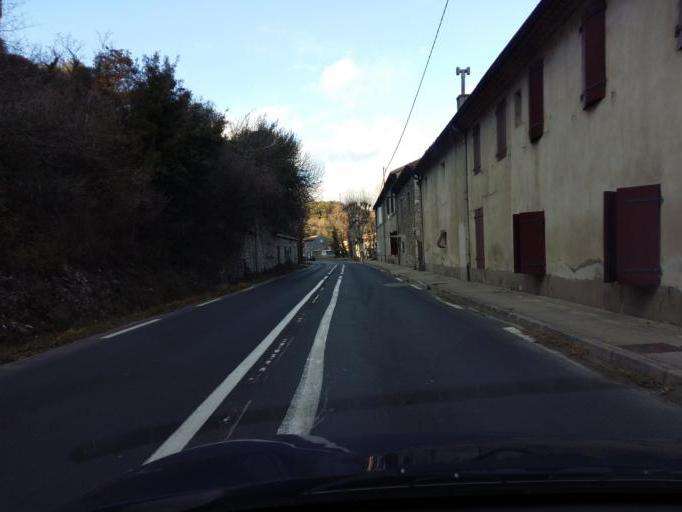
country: FR
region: Rhone-Alpes
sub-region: Departement de l'Ardeche
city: Le Teil
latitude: 44.5319
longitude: 4.6892
